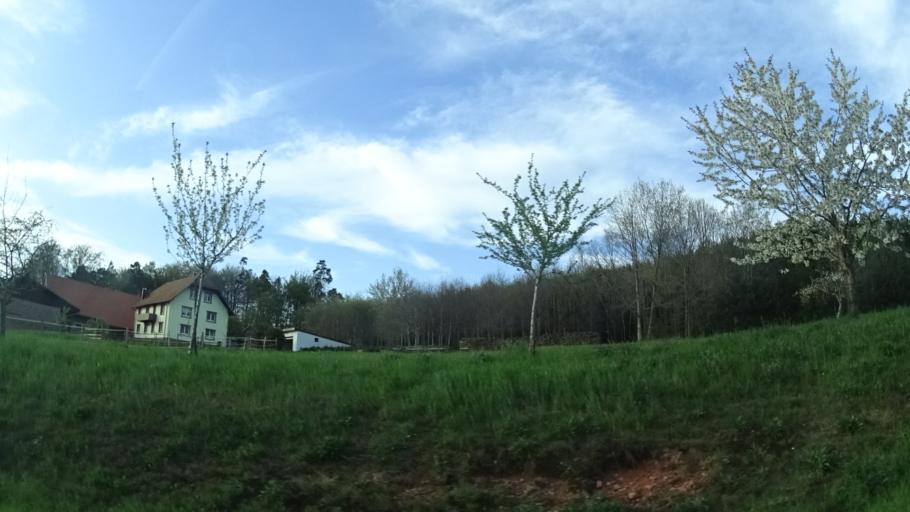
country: DE
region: Baden-Wuerttemberg
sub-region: Karlsruhe Region
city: Limbach
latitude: 49.4775
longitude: 9.1774
